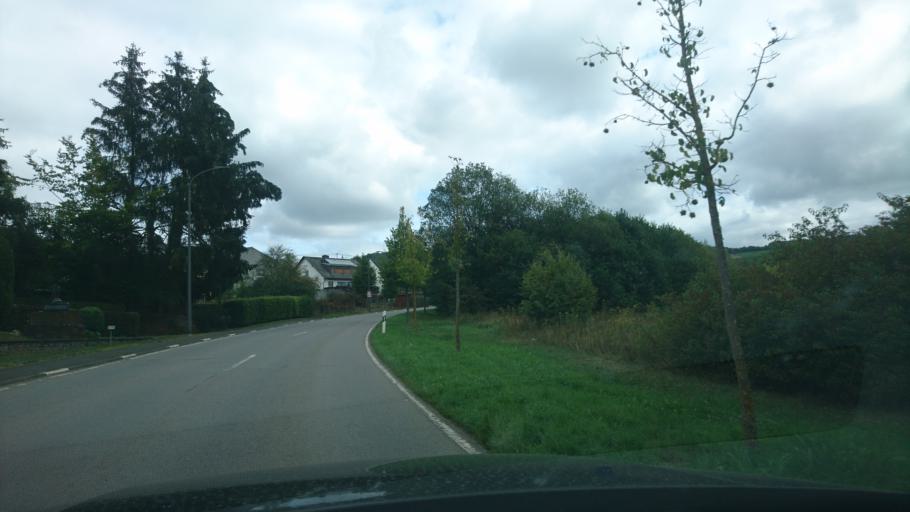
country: DE
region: Rheinland-Pfalz
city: Wiltingen
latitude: 49.6935
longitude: 6.6279
